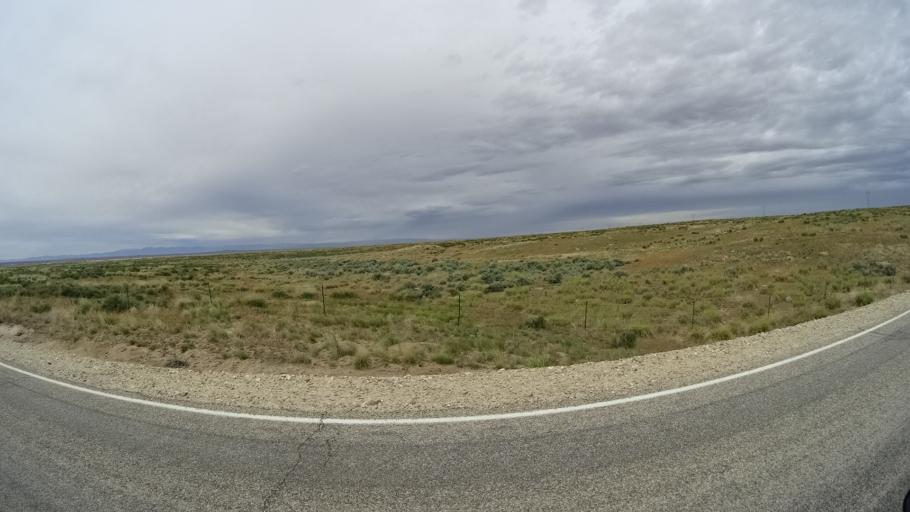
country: US
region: Idaho
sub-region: Ada County
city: Boise
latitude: 43.3645
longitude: -116.0051
